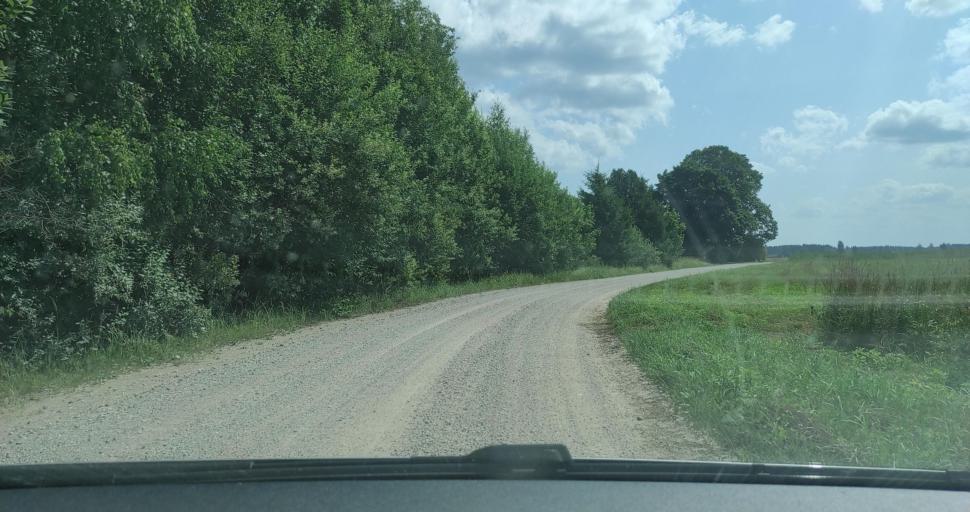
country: LV
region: Kuldigas Rajons
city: Kuldiga
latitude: 57.0575
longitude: 22.2406
